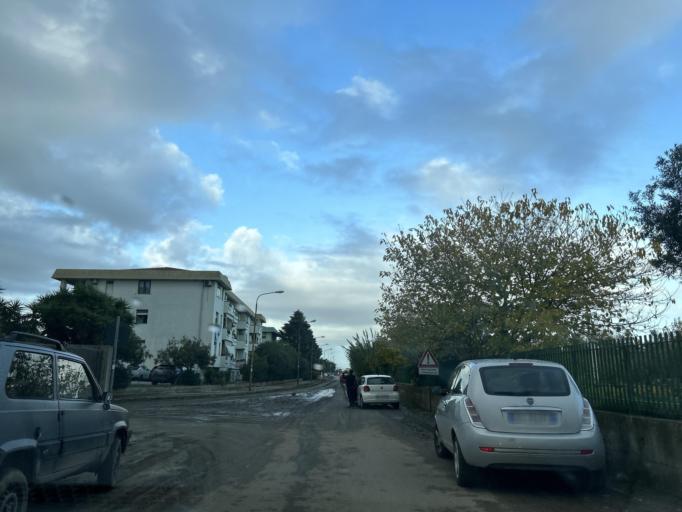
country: IT
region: Calabria
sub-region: Provincia di Catanzaro
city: Squillace Lido
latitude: 38.7775
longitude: 16.5706
